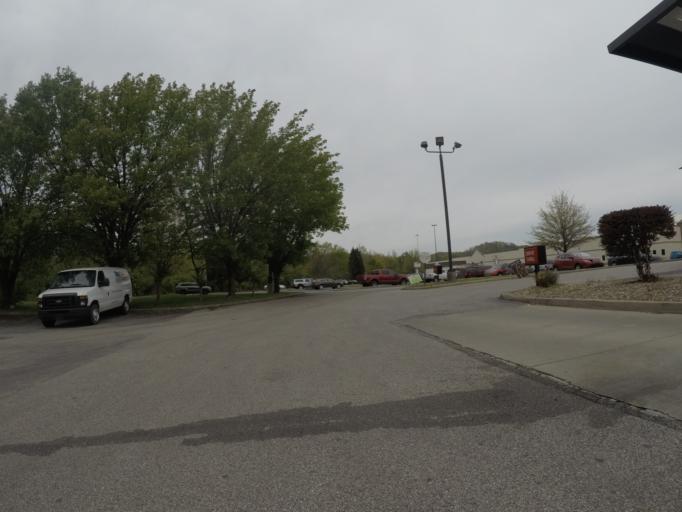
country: US
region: West Virginia
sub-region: Cabell County
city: Pea Ridge
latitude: 38.4139
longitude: -82.3468
